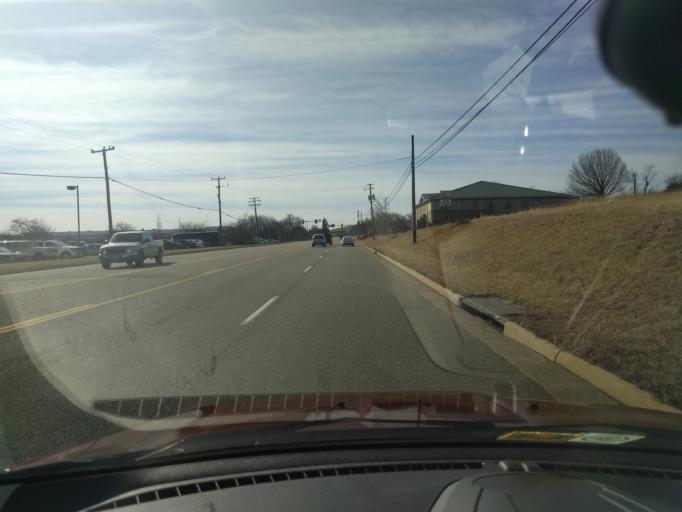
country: US
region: Virginia
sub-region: Augusta County
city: Verona
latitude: 38.1885
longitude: -79.0246
